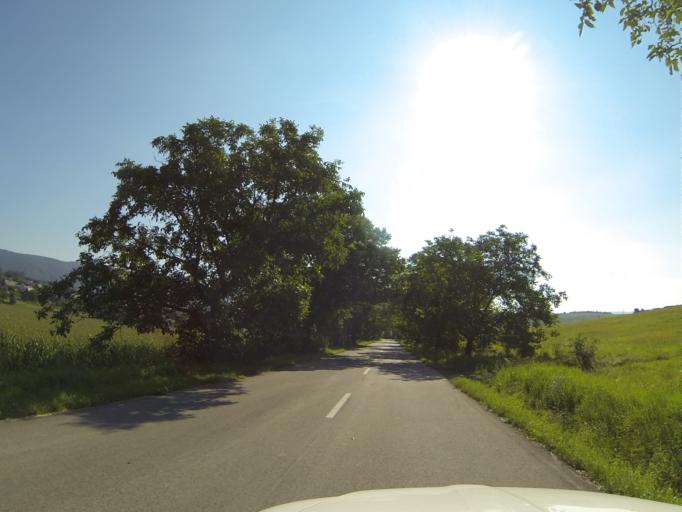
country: SK
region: Nitriansky
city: Handlova
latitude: 48.7764
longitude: 18.7043
